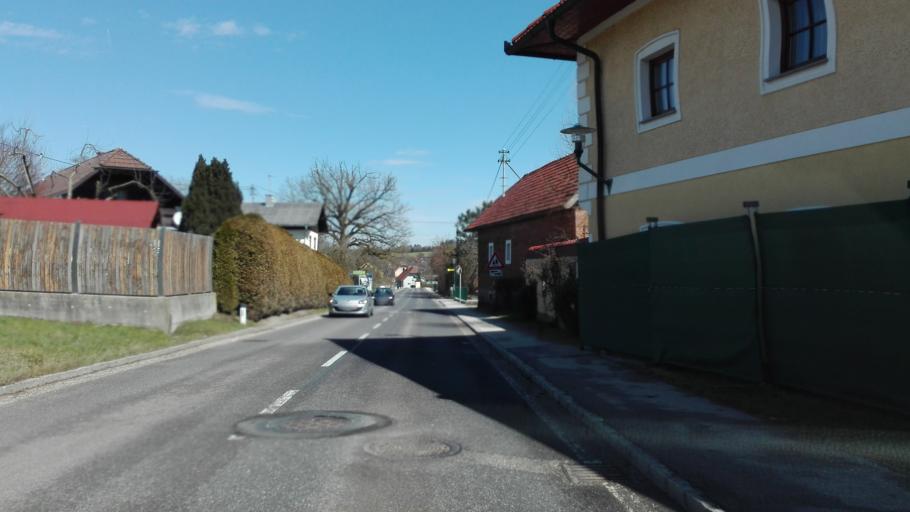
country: AT
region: Upper Austria
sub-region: Politischer Bezirk Grieskirchen
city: Bad Schallerbach
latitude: 48.1979
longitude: 13.9534
